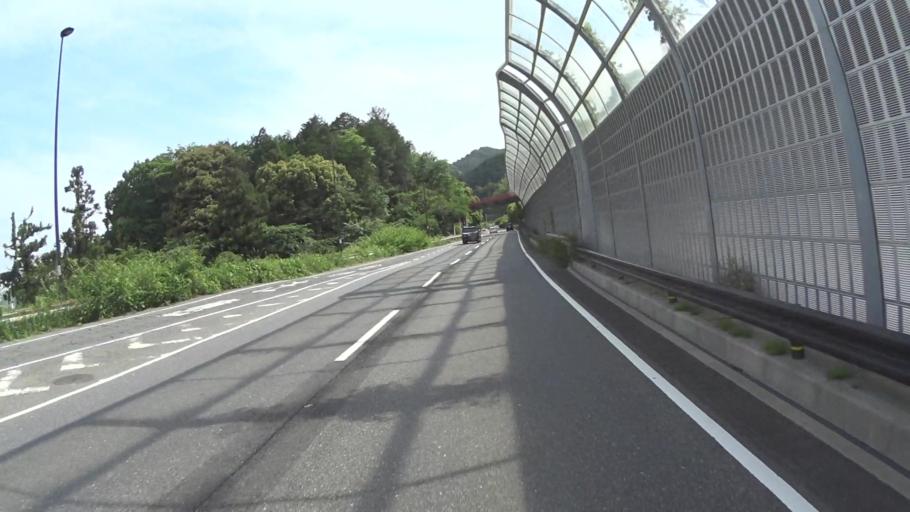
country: JP
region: Shiga Prefecture
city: Otsu-shi
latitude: 35.0251
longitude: 135.8500
